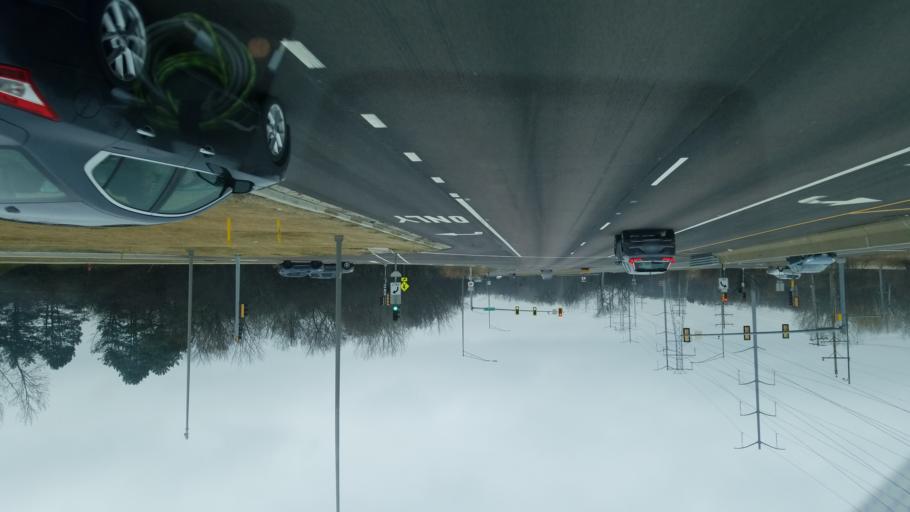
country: US
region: Illinois
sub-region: Lake County
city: Lake Forest
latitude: 42.2319
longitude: -87.8545
